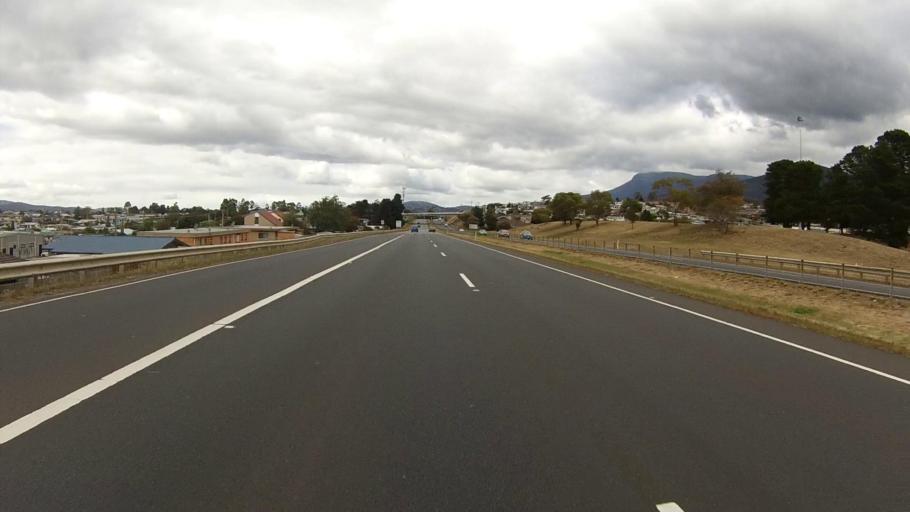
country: AU
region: Tasmania
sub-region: Glenorchy
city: Claremont
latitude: -42.7896
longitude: 147.2453
